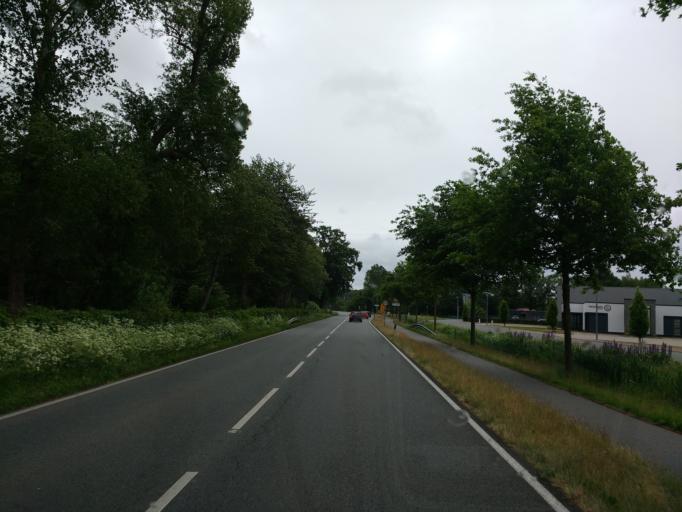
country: DE
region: Lower Saxony
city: Dinklage
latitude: 52.6679
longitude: 8.1408
